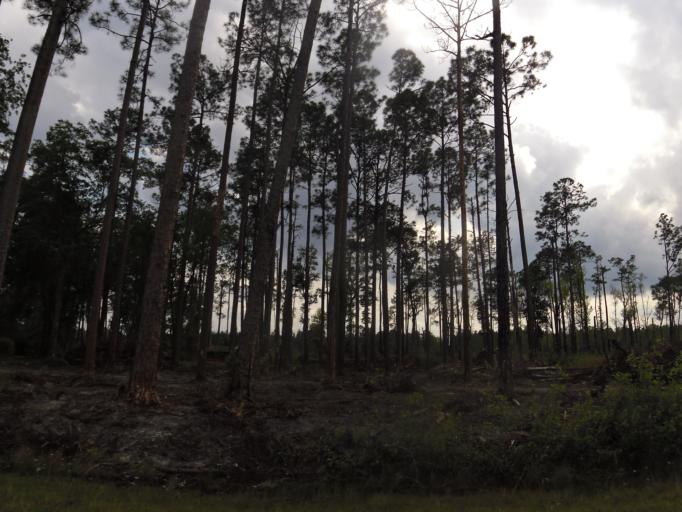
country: US
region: Georgia
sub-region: Charlton County
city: Folkston
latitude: 30.8076
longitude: -82.0477
